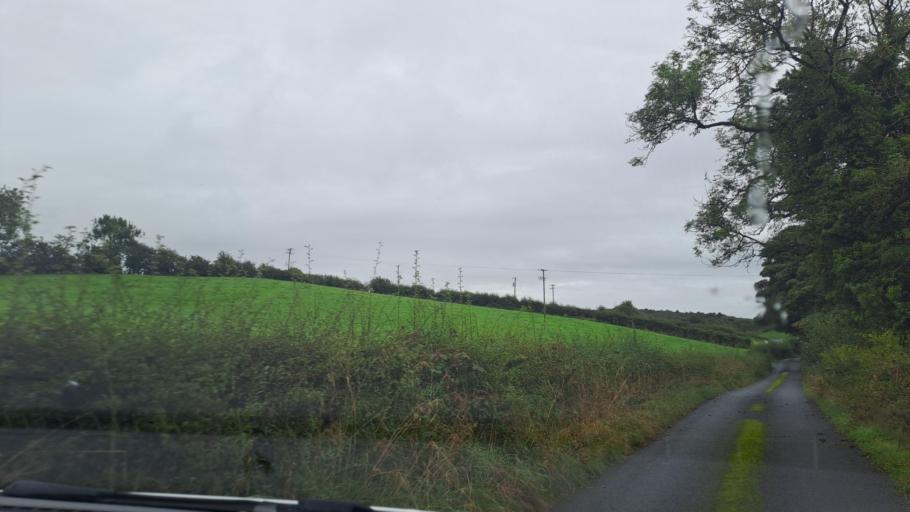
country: IE
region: Ulster
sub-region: An Cabhan
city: Kingscourt
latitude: 53.9727
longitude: -6.8483
